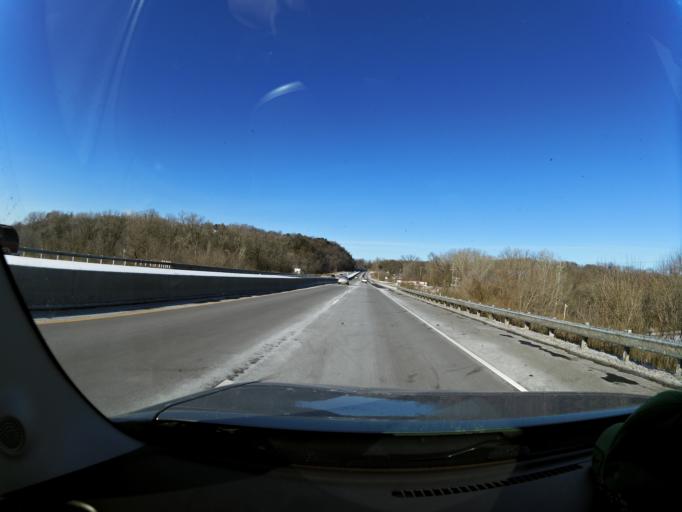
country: US
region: Minnesota
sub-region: Dakota County
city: Hastings
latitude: 44.7555
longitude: -92.8532
